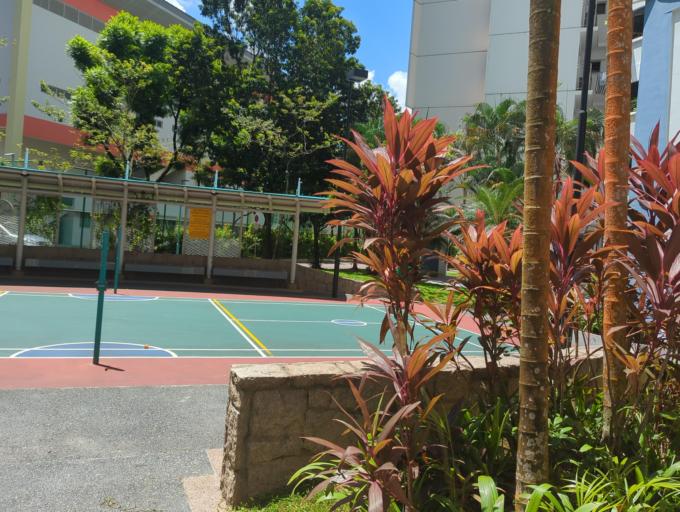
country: MY
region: Johor
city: Kampung Pasir Gudang Baru
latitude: 1.3924
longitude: 103.8921
